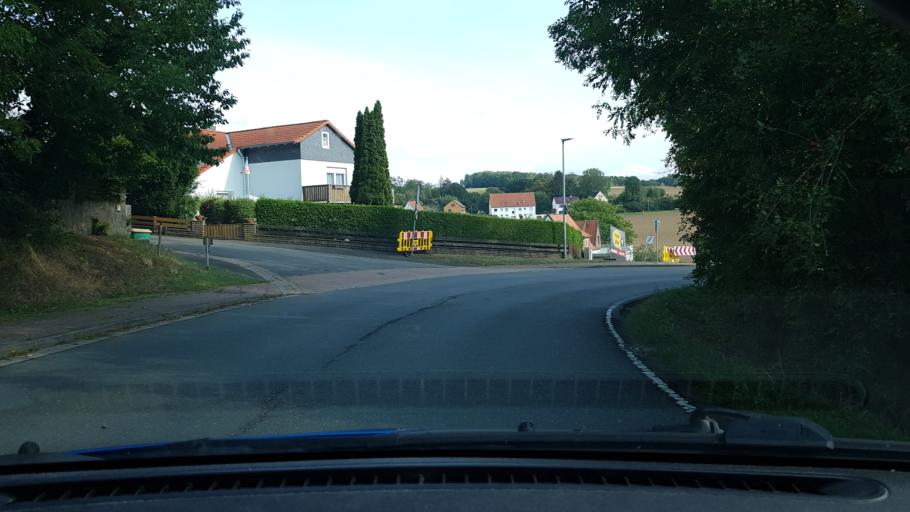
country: DE
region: Lower Saxony
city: Messenkamp
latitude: 52.2392
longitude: 9.4272
